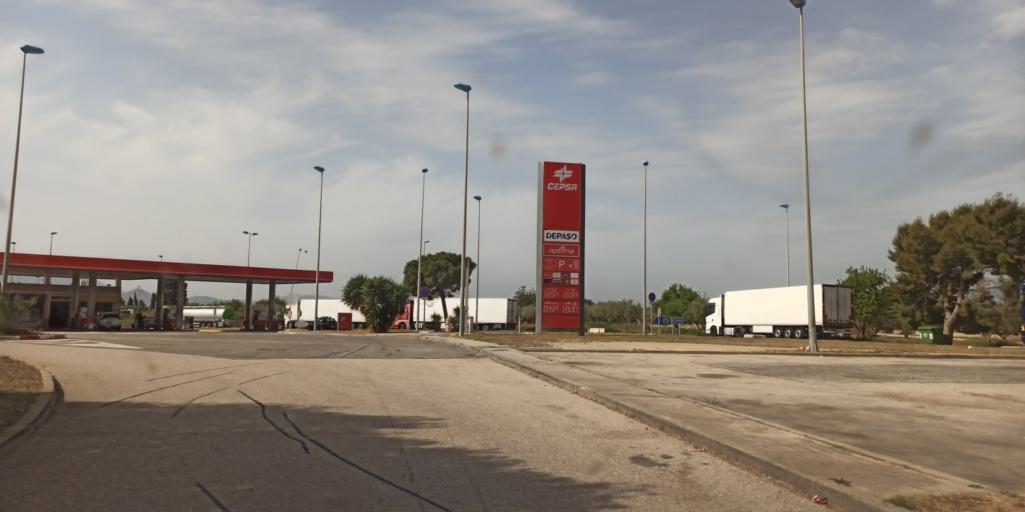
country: ES
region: Catalonia
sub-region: Provincia de Tarragona
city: Camarles
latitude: 40.7659
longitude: 0.6266
